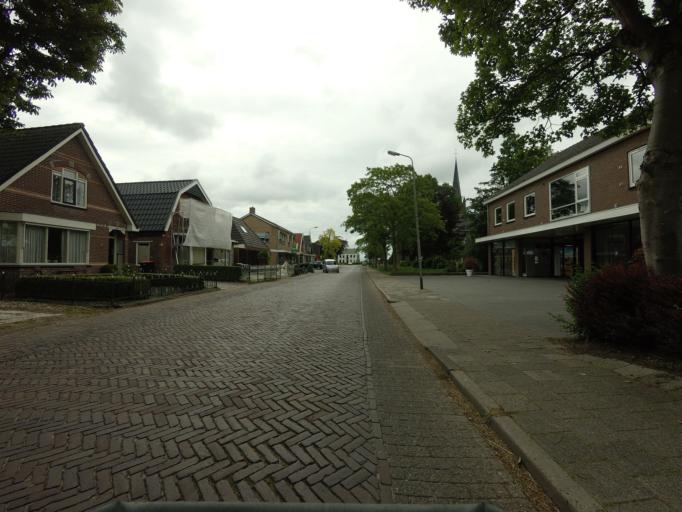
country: NL
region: North Holland
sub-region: Gemeente Hoorn
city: Hoorn
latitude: 52.6911
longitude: 5.0585
